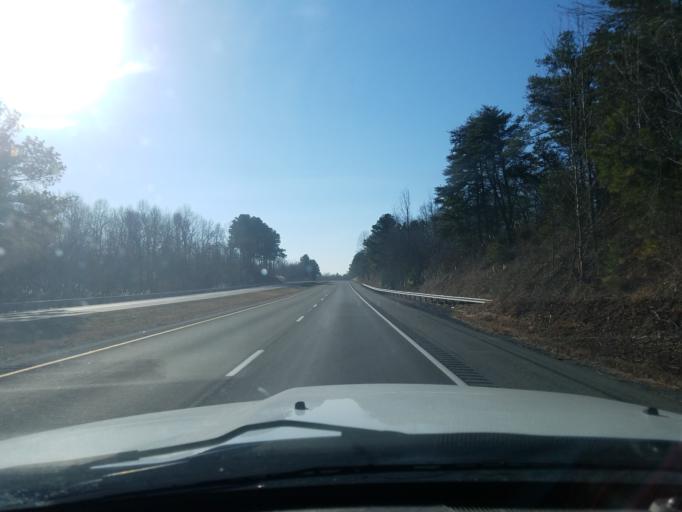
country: US
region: Kentucky
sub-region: Muhlenberg County
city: Central City
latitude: 37.2991
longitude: -87.0734
